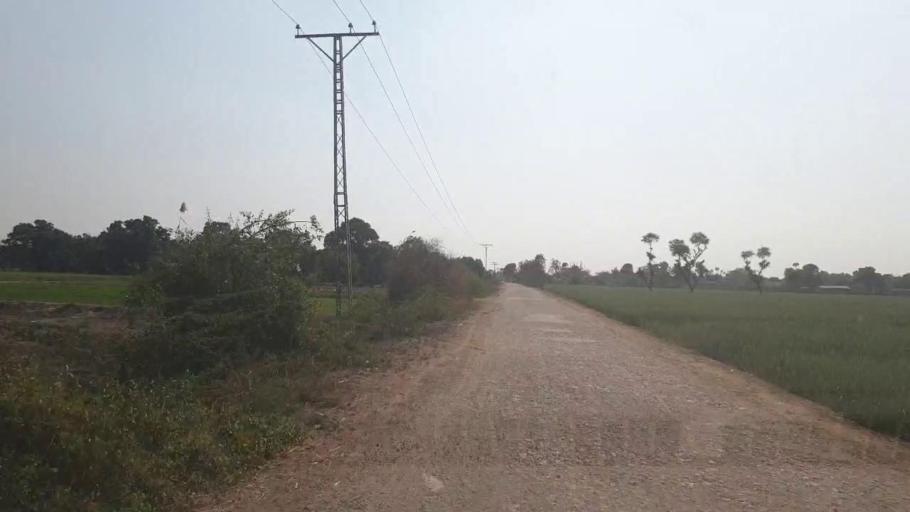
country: PK
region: Sindh
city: Mirpur Khas
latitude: 25.4927
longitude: 68.8820
